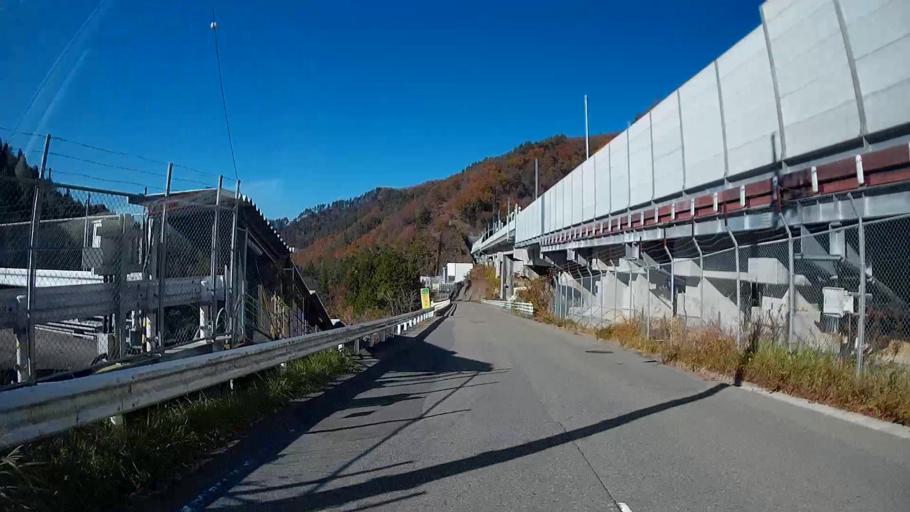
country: JP
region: Yamanashi
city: Otsuki
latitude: 35.5633
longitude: 139.0044
